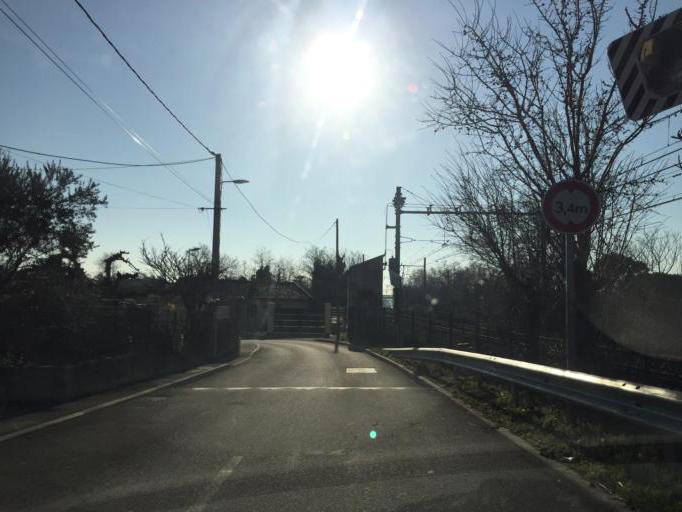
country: FR
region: Provence-Alpes-Cote d'Azur
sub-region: Departement du Vaucluse
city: Sorgues
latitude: 44.0103
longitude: 4.8779
